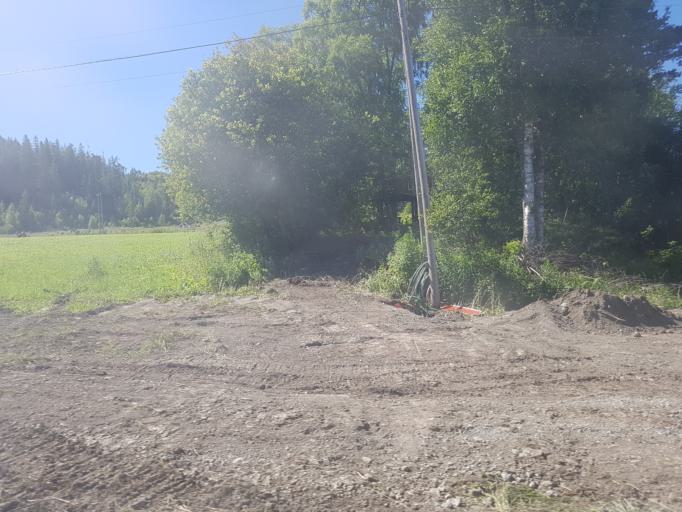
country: NO
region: Sor-Trondelag
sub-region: Skaun
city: Borsa
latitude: 63.4411
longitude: 10.1966
